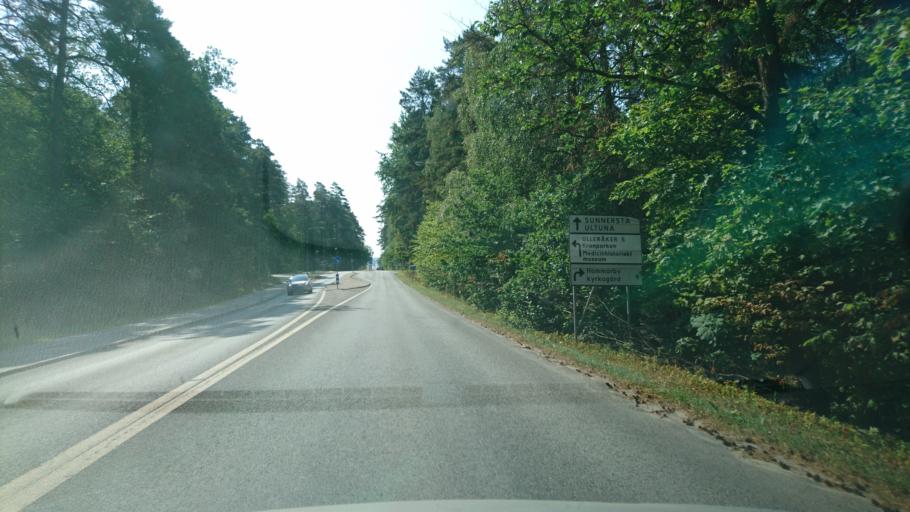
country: SE
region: Uppsala
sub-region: Uppsala Kommun
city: Uppsala
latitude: 59.8292
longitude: 17.6438
